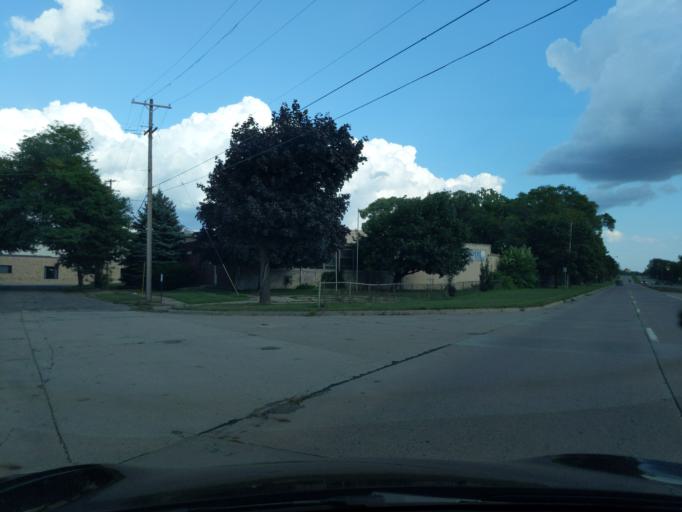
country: US
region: Michigan
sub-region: Jackson County
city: Jackson
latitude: 42.2413
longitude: -84.3995
